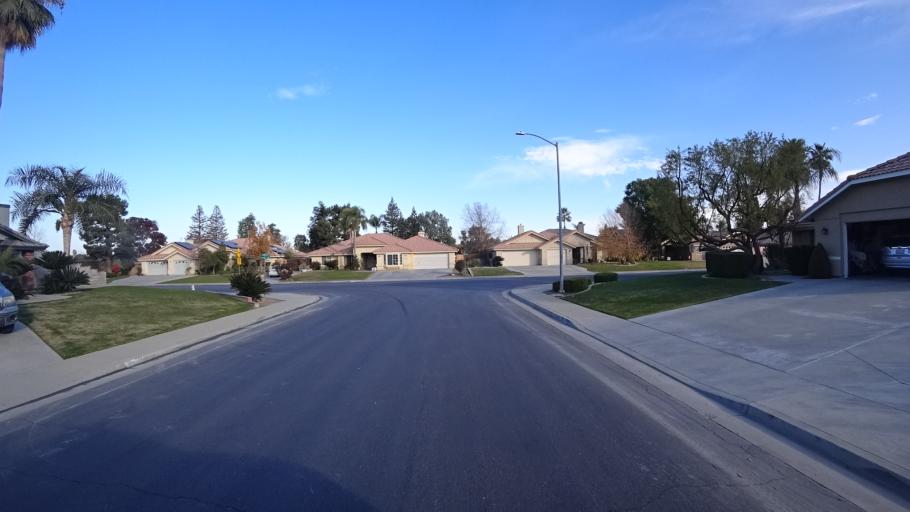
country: US
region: California
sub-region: Kern County
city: Rosedale
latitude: 35.3486
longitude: -119.1583
